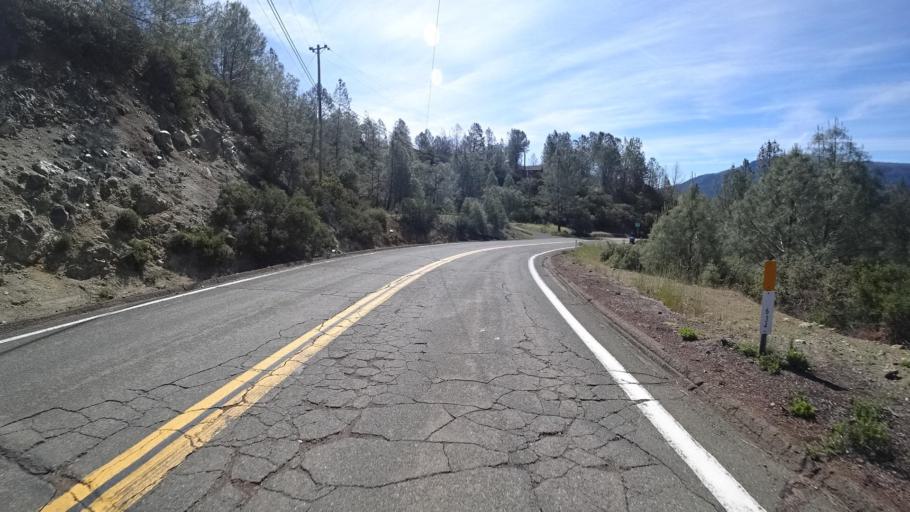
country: US
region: California
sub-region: Lake County
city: Cobb
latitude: 38.8675
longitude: -122.7673
